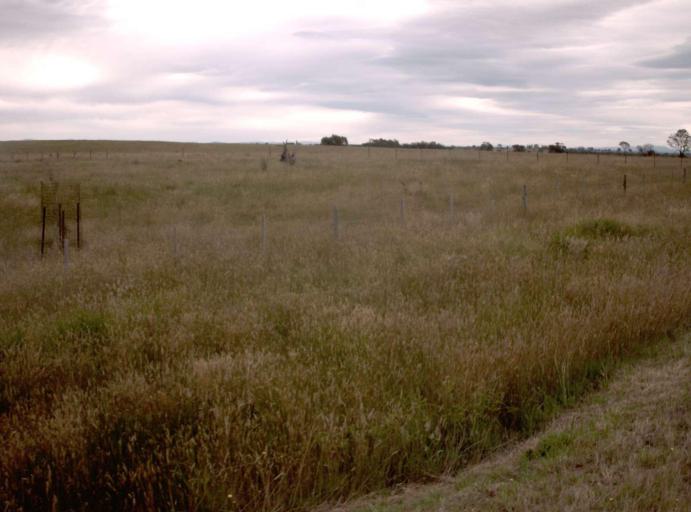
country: AU
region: Victoria
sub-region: East Gippsland
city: Bairnsdale
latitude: -38.0006
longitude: 147.3975
